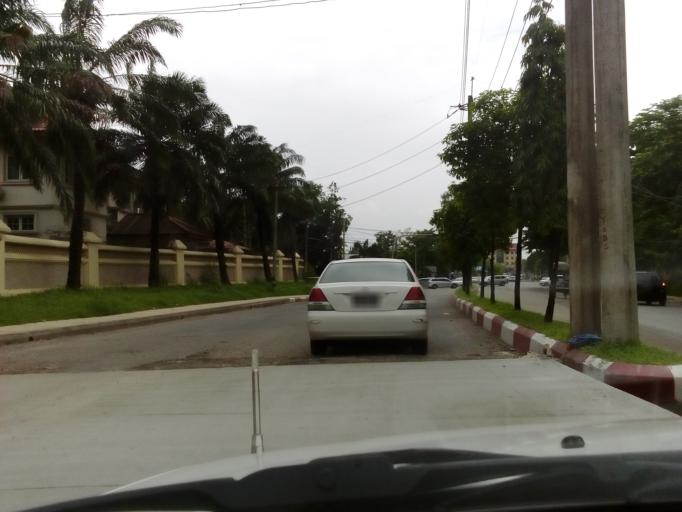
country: MM
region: Yangon
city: Yangon
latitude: 16.8668
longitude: 96.1331
